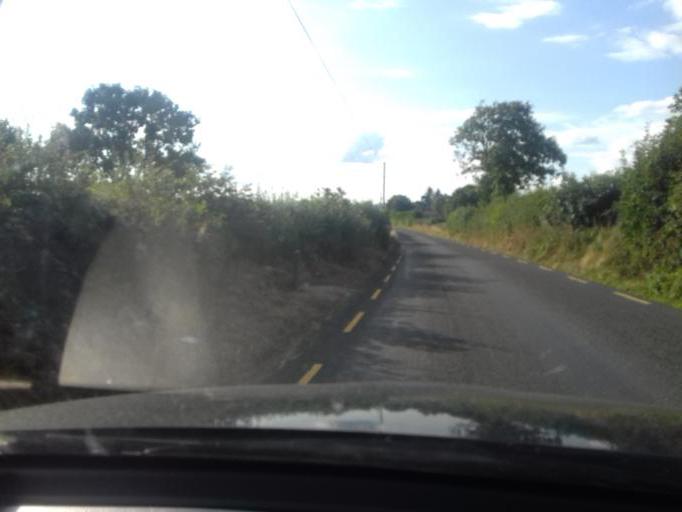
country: IE
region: Leinster
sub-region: Kilkenny
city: Graiguenamanagh
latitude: 52.5978
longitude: -6.9897
